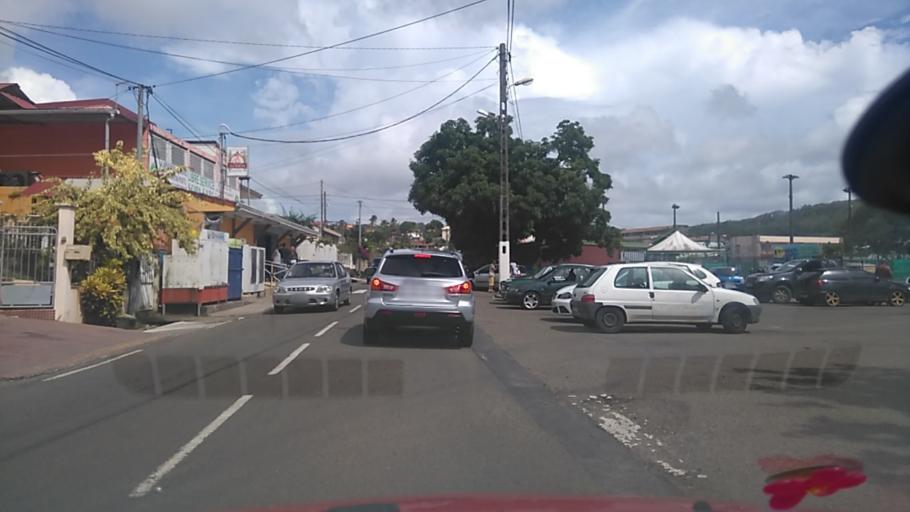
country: MQ
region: Martinique
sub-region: Martinique
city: Saint-Esprit
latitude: 14.5655
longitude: -60.9356
